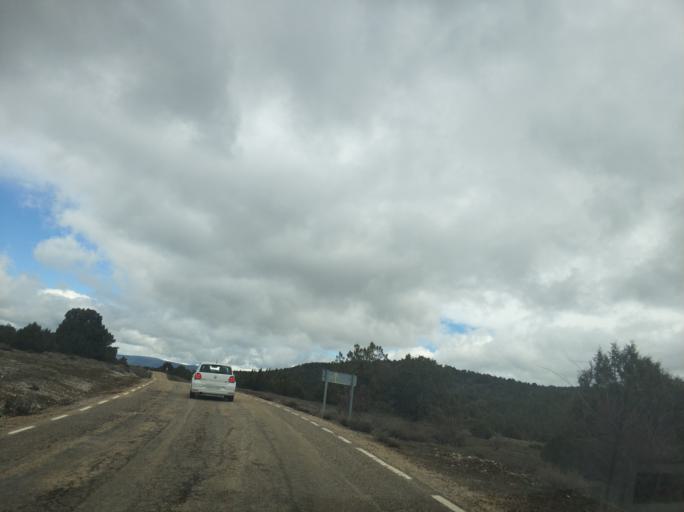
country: ES
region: Castille and Leon
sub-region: Provincia de Soria
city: Abejar
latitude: 41.7867
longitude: -2.7693
